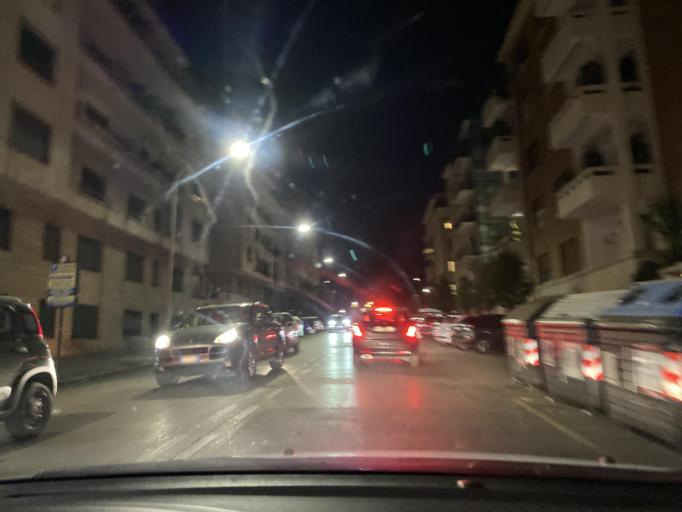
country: VA
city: Vatican City
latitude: 41.9215
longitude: 12.4818
